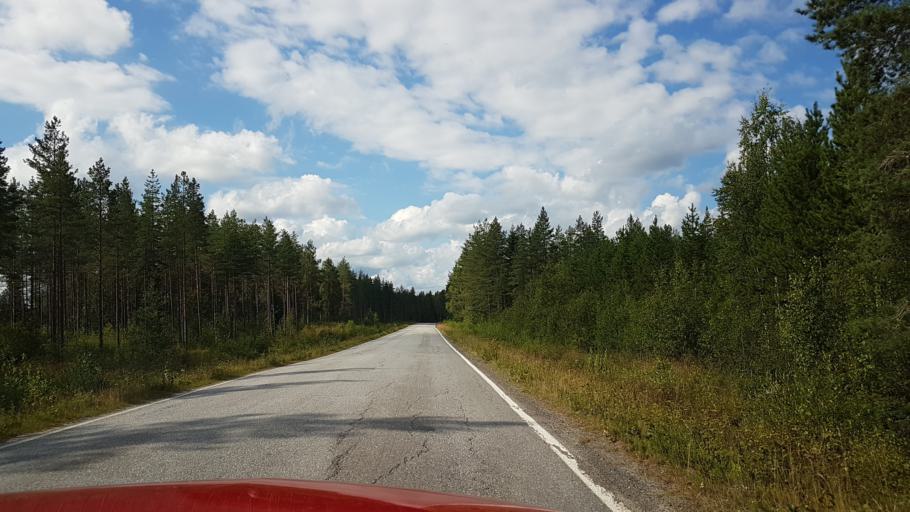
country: FI
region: Northern Ostrobothnia
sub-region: Ylivieska
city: Himanka
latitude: 64.0781
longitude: 23.7168
